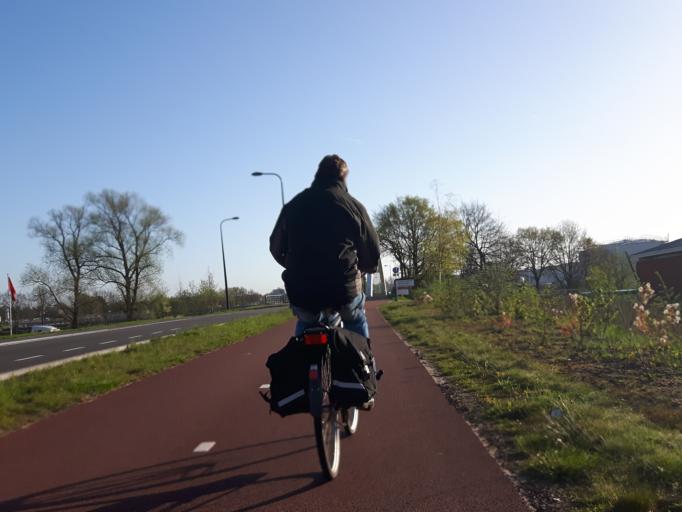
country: NL
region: Overijssel
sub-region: Gemeente Enschede
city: Enschede
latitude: 52.2308
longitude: 6.8399
